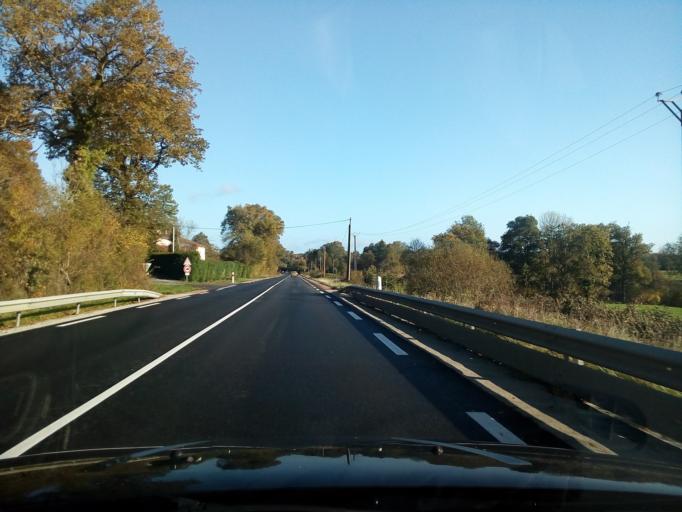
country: FR
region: Limousin
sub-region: Departement de la Haute-Vienne
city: Magnac-Laval
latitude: 46.1552
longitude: 1.1290
